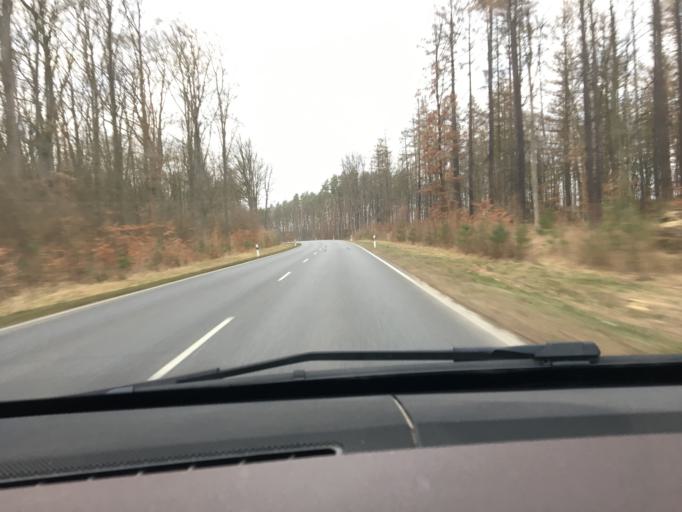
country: DE
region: Brandenburg
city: Liebenwalde
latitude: 52.8723
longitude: 13.4890
